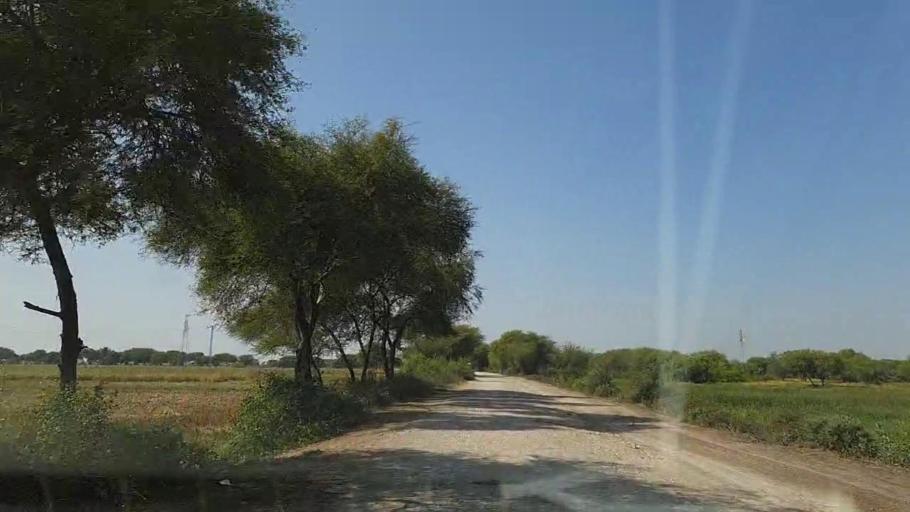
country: PK
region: Sindh
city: Chuhar Jamali
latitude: 24.4170
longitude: 68.0289
